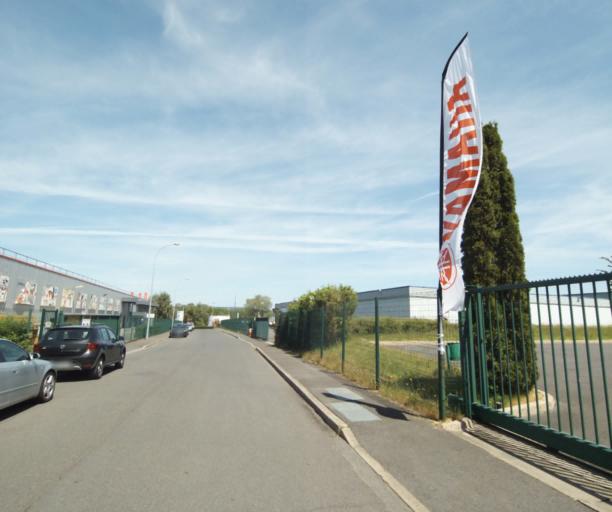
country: FR
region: Champagne-Ardenne
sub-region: Departement des Ardennes
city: Charleville-Mezieres
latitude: 49.7538
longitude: 4.7100
